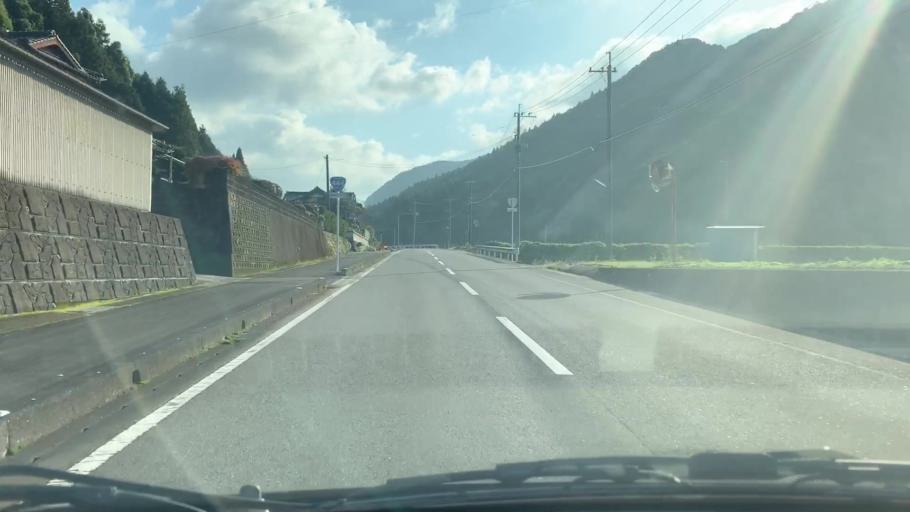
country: JP
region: Saga Prefecture
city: Kashima
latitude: 33.0615
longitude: 130.0701
